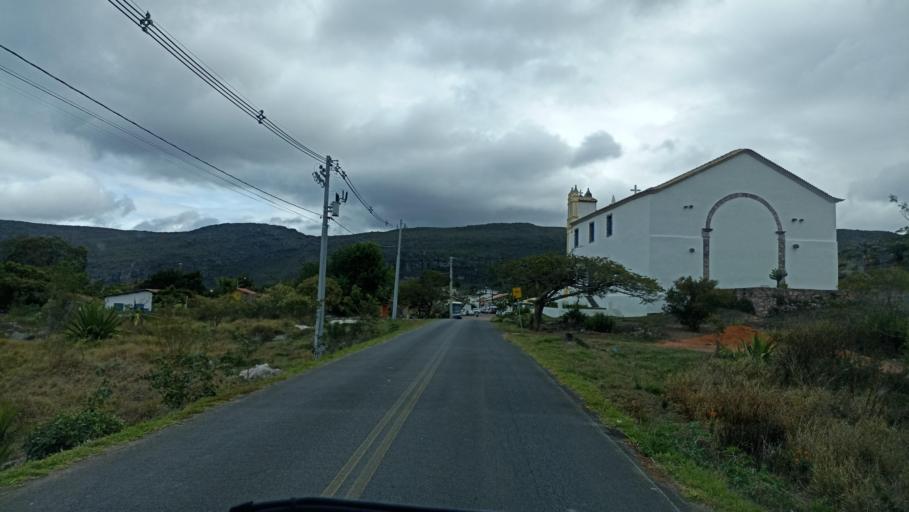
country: BR
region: Bahia
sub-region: Andarai
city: Vera Cruz
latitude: -13.0031
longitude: -41.3669
